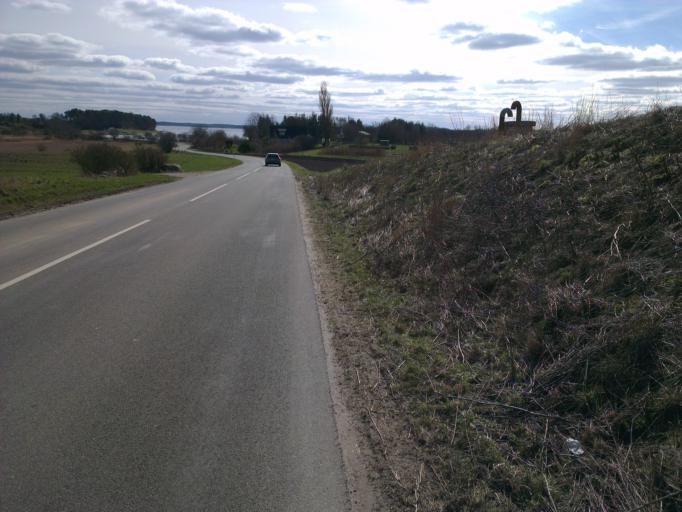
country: DK
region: Capital Region
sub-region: Frederikssund Kommune
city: Skibby
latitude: 55.7452
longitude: 11.9867
